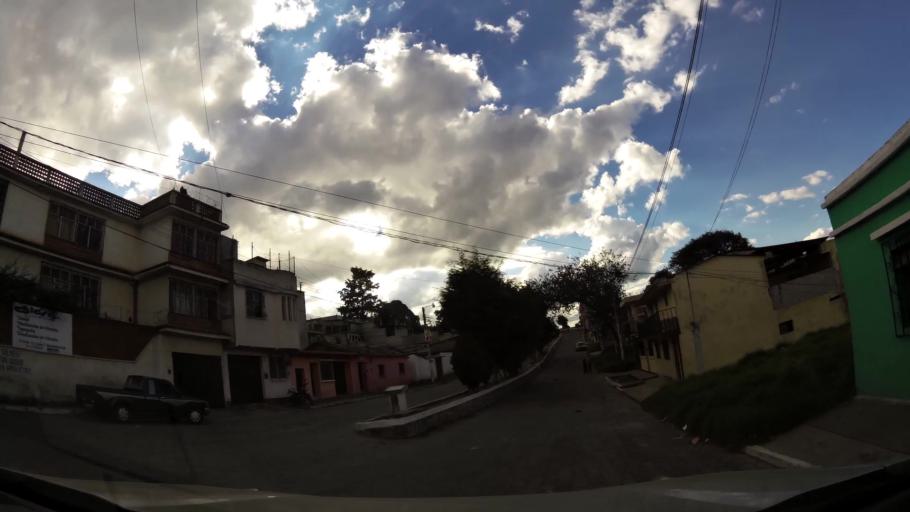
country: GT
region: Quetzaltenango
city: Quetzaltenango
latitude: 14.8487
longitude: -91.5192
